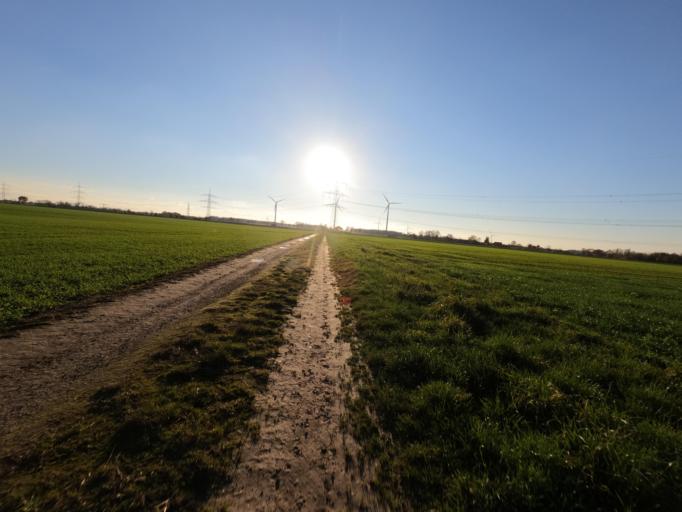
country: DE
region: North Rhine-Westphalia
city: Geilenkirchen
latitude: 51.0157
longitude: 6.1243
